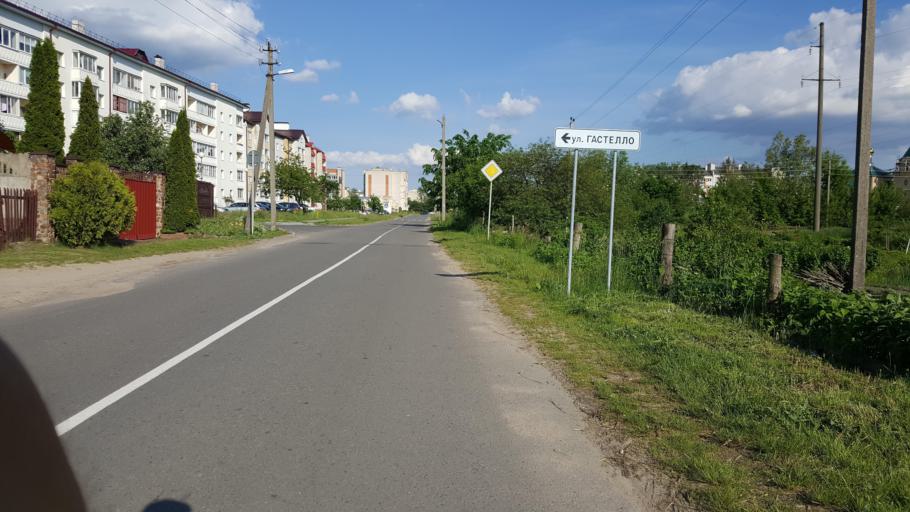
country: BY
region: Brest
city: Kamyanyets
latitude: 52.3932
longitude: 23.8187
